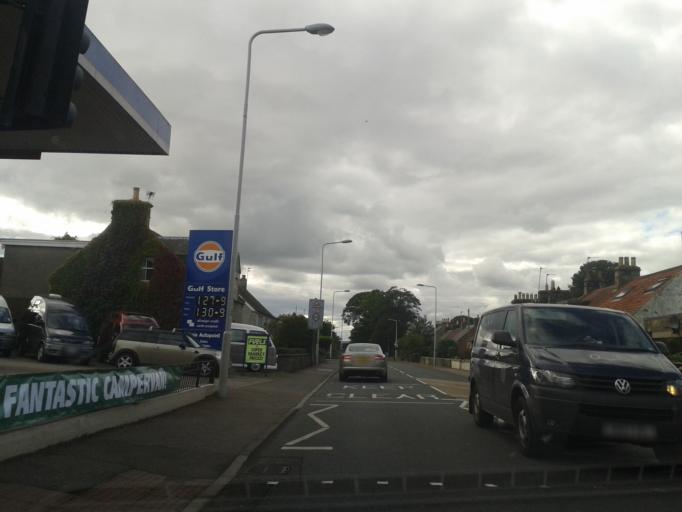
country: GB
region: Scotland
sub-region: Fife
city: Balmullo
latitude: 56.3447
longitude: -2.9512
